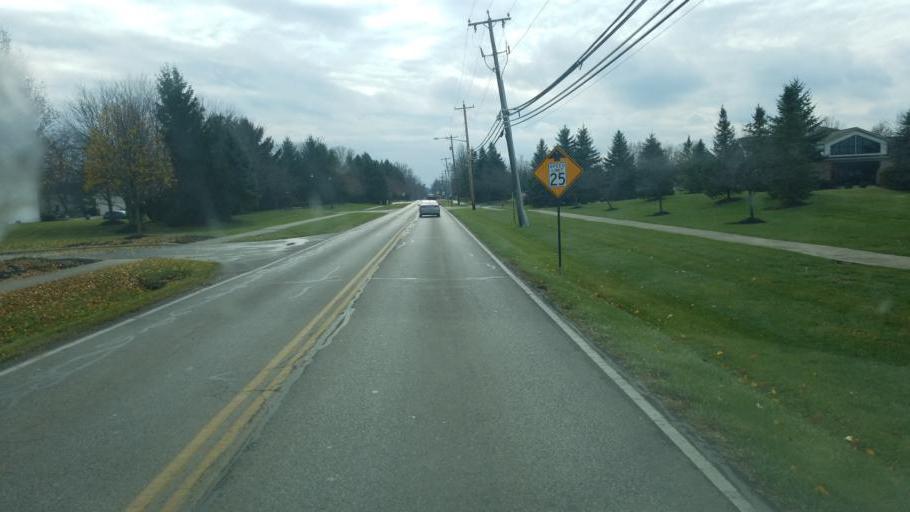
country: US
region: Ohio
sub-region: Delaware County
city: Powell
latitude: 40.1672
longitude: -83.0767
